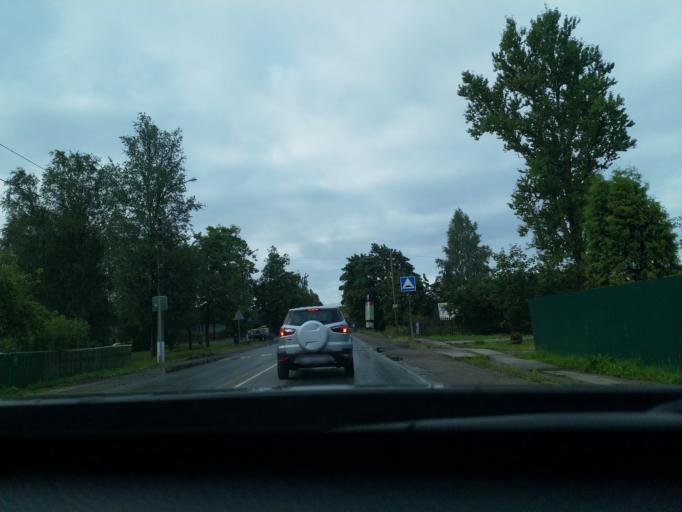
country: RU
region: Leningrad
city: Nikol'skoye
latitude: 59.6927
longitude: 30.7850
